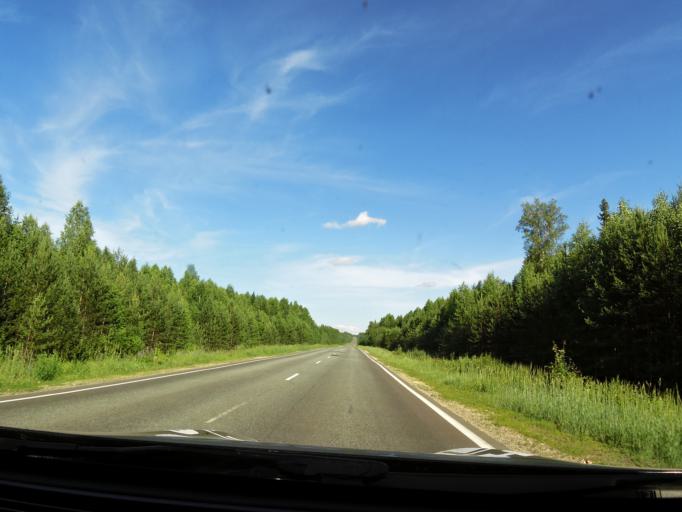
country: RU
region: Kirov
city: Dubrovka
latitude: 58.9043
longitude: 51.2741
